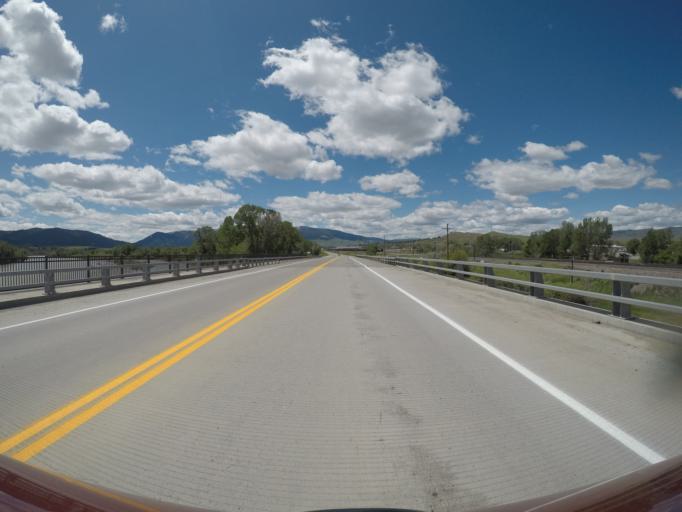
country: US
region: Montana
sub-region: Park County
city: Livingston
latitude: 45.6745
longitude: -110.5378
